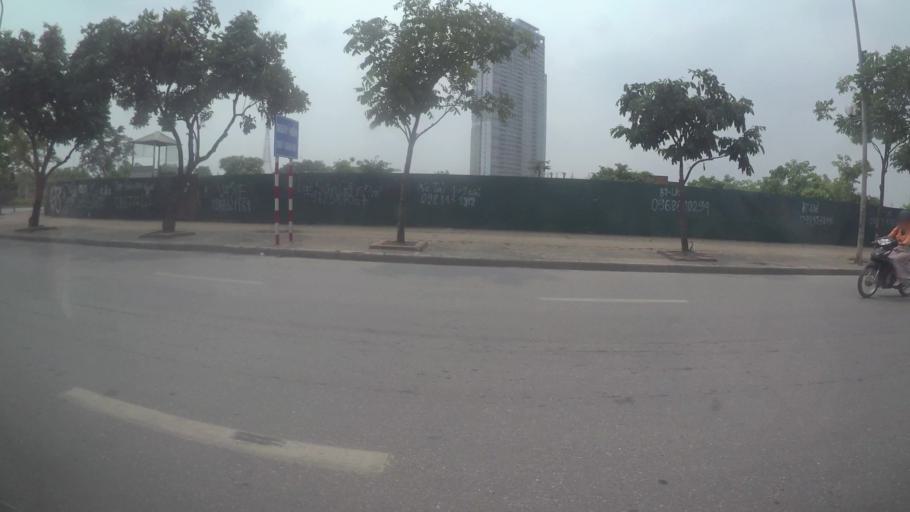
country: VN
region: Ha Noi
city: Thanh Xuan
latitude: 21.0055
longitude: 105.7732
